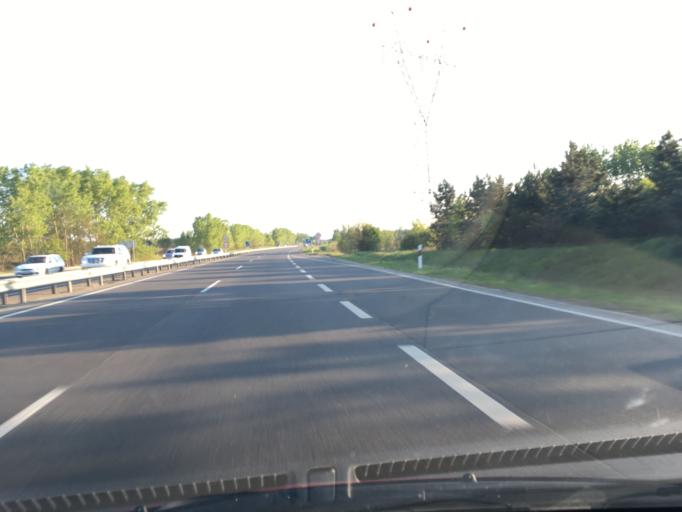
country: HU
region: Pest
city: God
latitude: 47.6816
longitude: 19.1740
